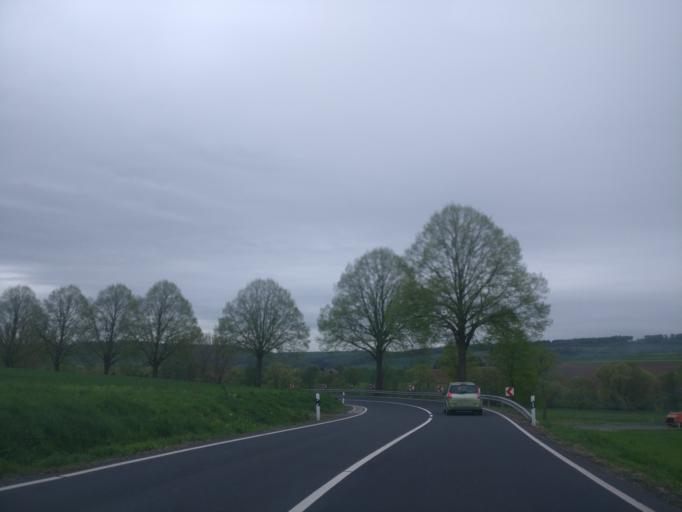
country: DE
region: Lower Saxony
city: Scheden
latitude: 51.4646
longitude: 9.7211
